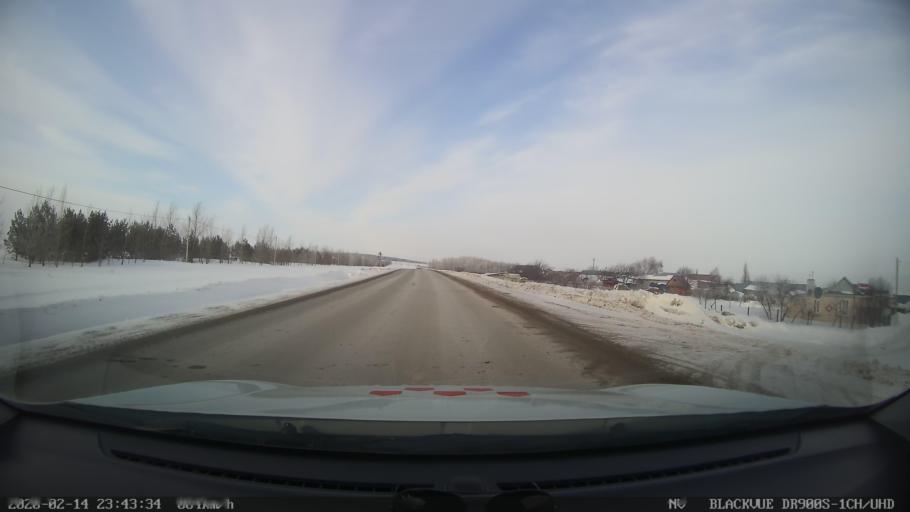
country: RU
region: Tatarstan
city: Kuybyshevskiy Zaton
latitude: 55.2033
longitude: 49.2494
